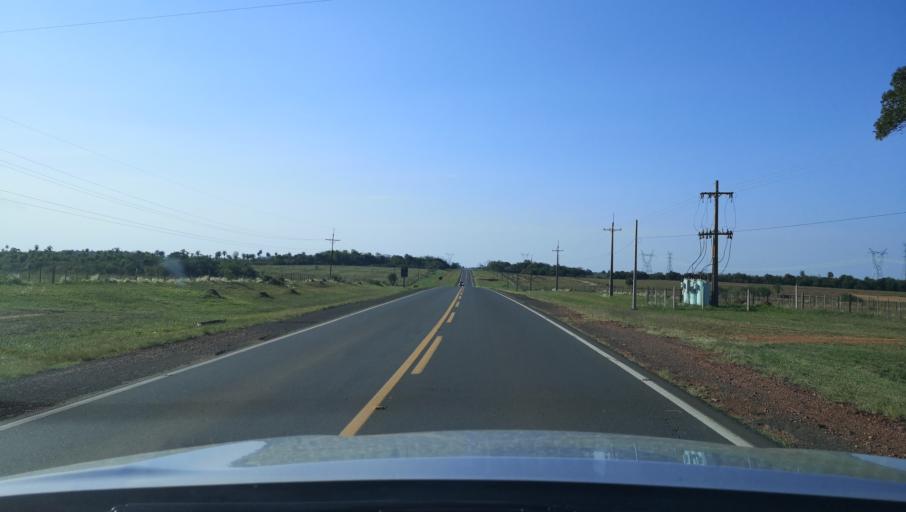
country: PY
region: Misiones
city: Santa Maria
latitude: -26.8055
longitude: -57.0202
